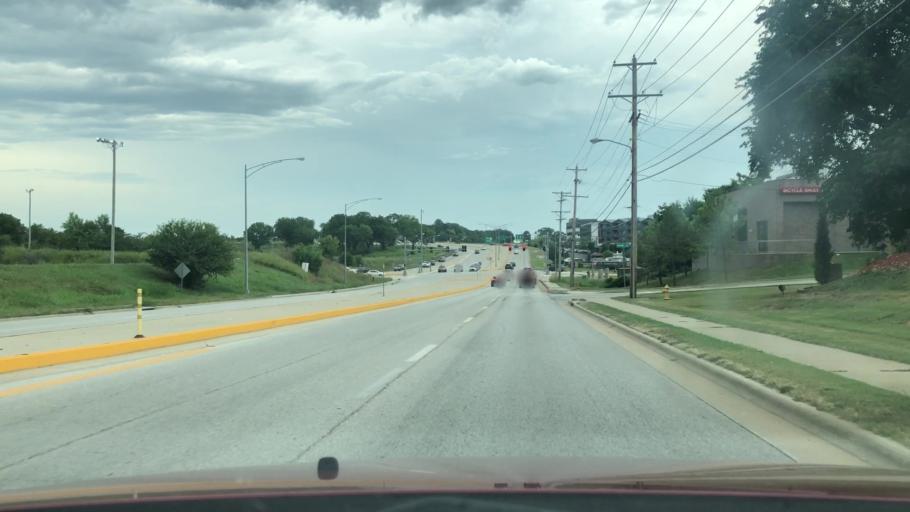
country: US
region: Missouri
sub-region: Greene County
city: Springfield
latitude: 37.1371
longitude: -93.2590
